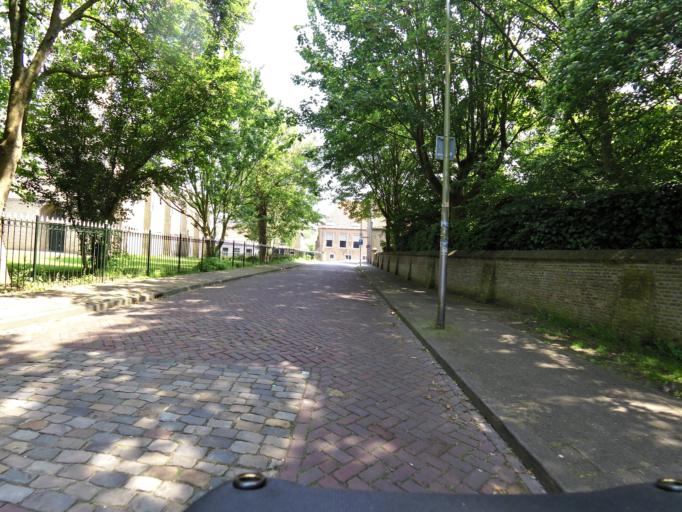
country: NL
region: South Holland
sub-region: Gemeente Maassluis
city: Maassluis
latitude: 51.8643
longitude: 4.2434
